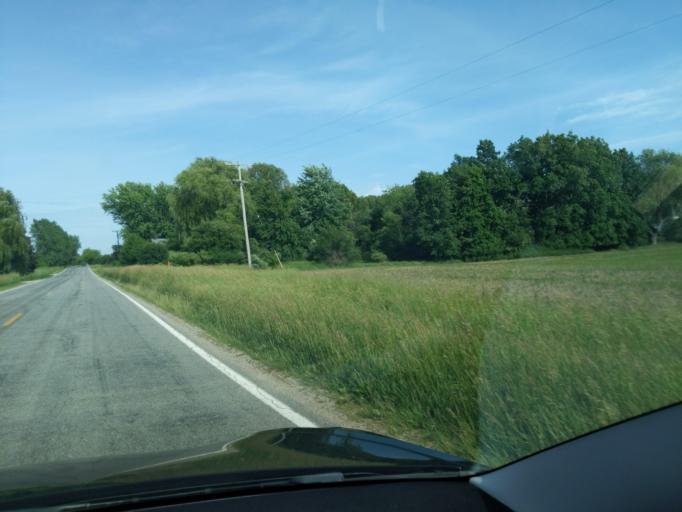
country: US
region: Michigan
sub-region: Newaygo County
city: Fremont
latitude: 43.4239
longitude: -85.9942
